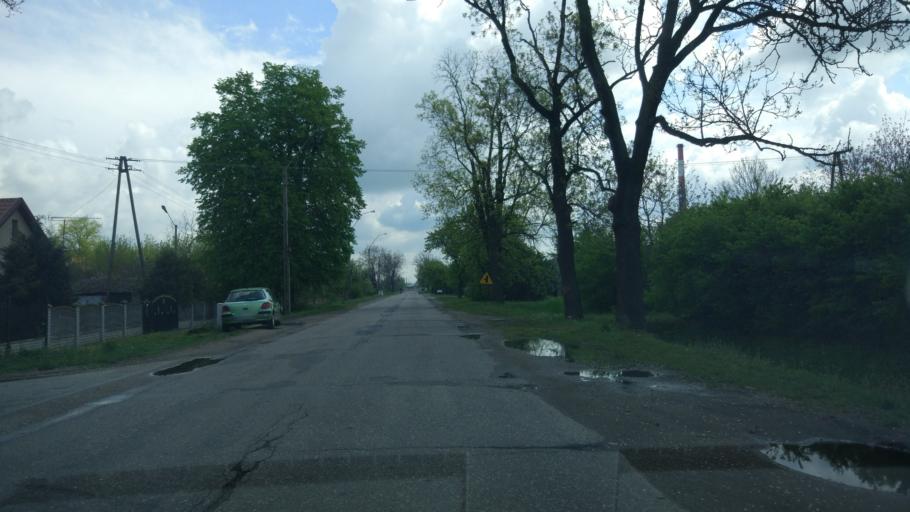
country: PL
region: Lodz Voivodeship
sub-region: Powiat kutnowski
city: Kutno
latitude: 52.2262
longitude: 19.3990
